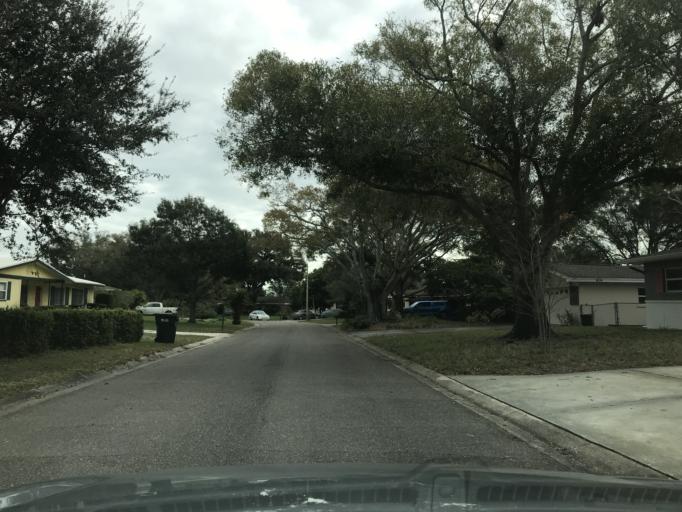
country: US
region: Florida
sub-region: Pinellas County
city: Belleair
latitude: 27.9334
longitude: -82.7825
